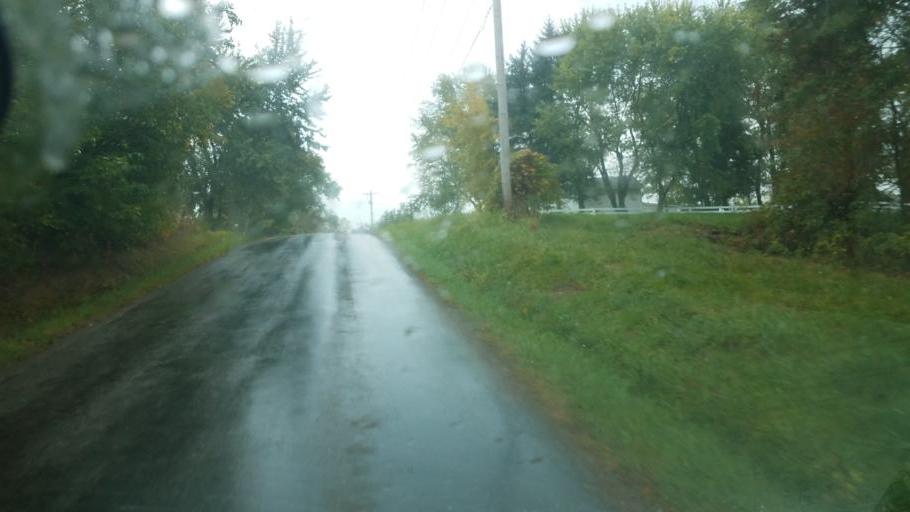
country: US
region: Ohio
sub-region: Ashland County
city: Ashland
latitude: 40.8092
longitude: -82.3497
